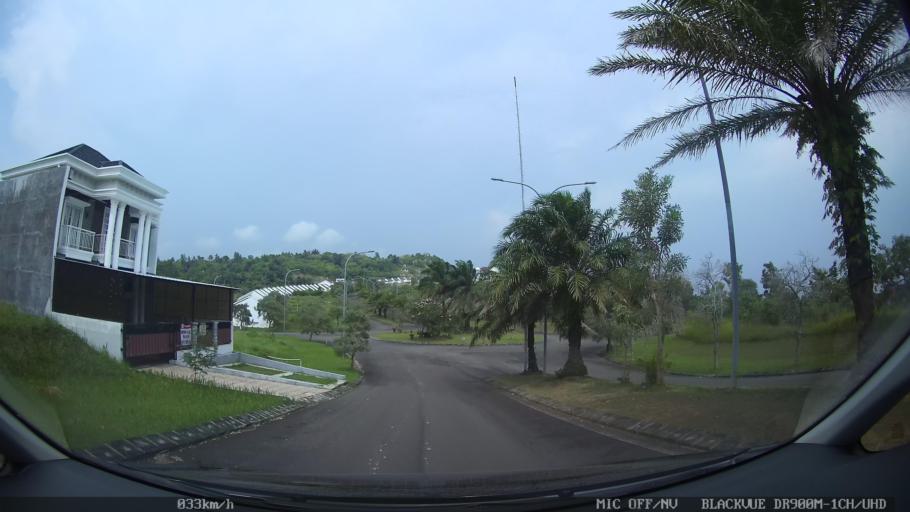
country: ID
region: Lampung
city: Bandarlampung
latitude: -5.4311
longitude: 105.2830
